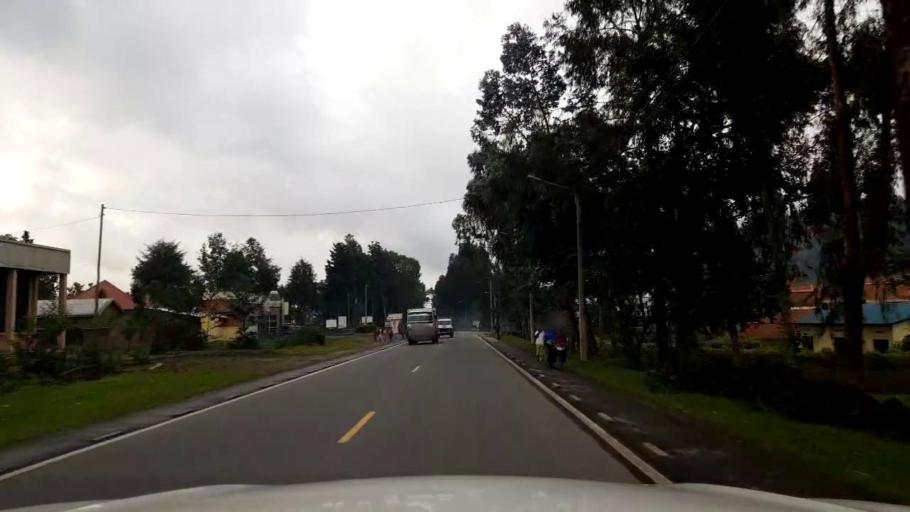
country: RW
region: Northern Province
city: Musanze
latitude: -1.5571
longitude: 29.5542
